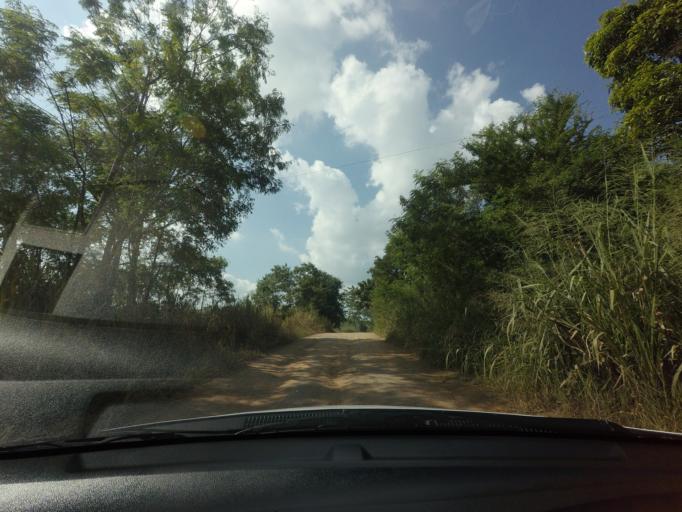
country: TH
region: Nakhon Ratchasima
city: Wang Nam Khiao
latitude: 14.4996
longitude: 101.6305
